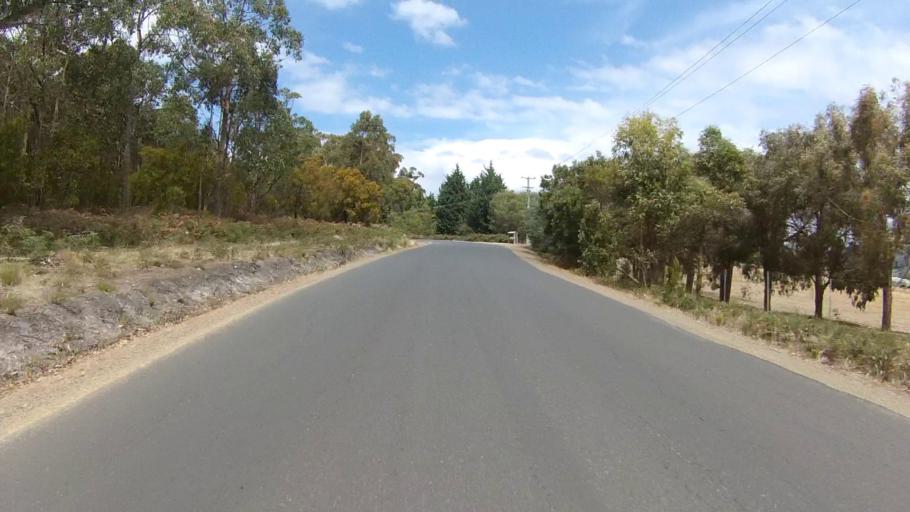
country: AU
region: Tasmania
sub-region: Kingborough
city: Blackmans Bay
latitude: -43.0118
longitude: 147.2883
